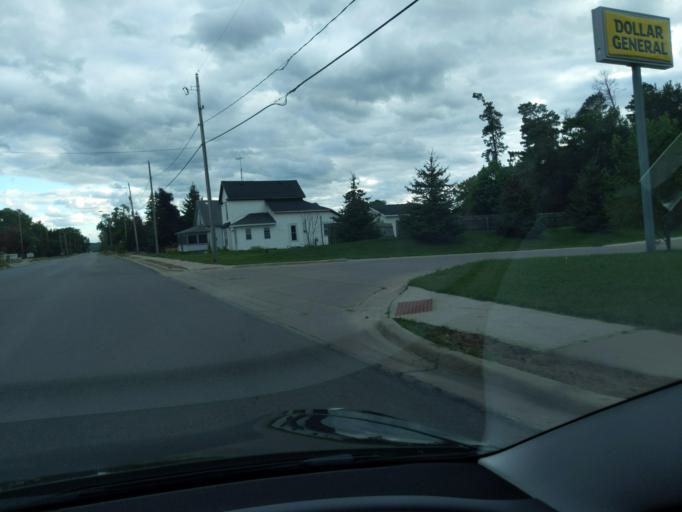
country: US
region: Michigan
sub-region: Kalkaska County
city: Rapid City
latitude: 44.8315
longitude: -85.2828
